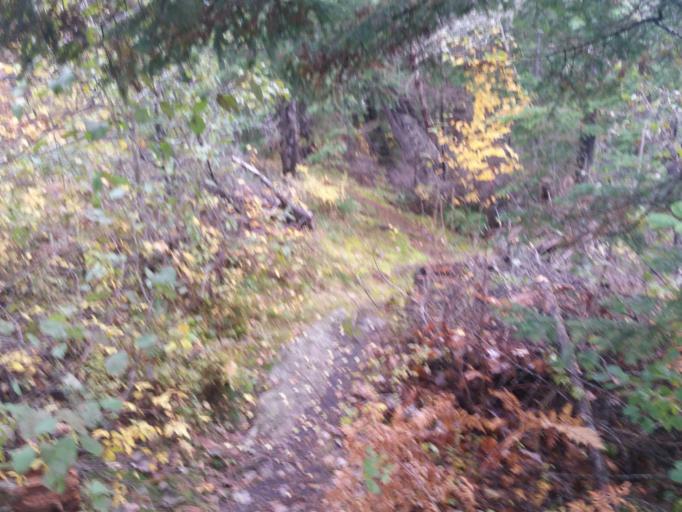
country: CA
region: Ontario
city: Deep River
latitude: 45.9934
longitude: -77.4018
